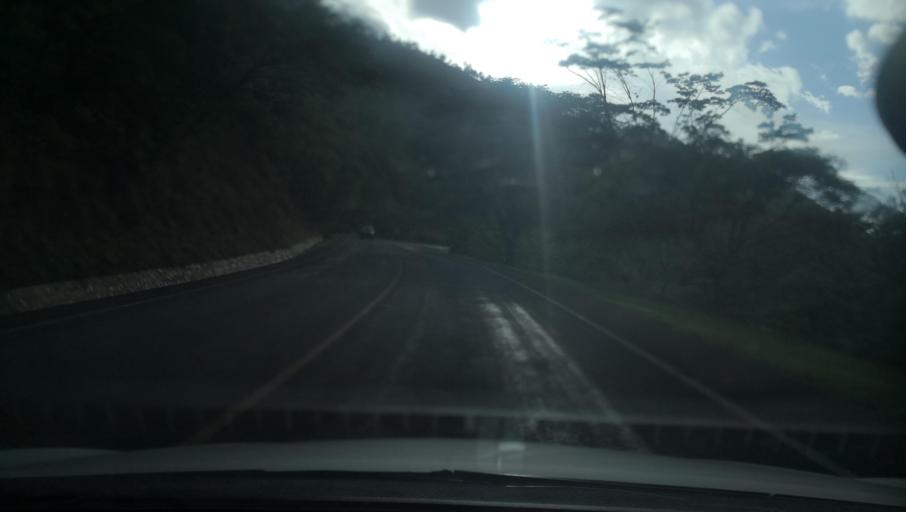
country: NI
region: Nueva Segovia
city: Mozonte
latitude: 13.6994
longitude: -86.4894
